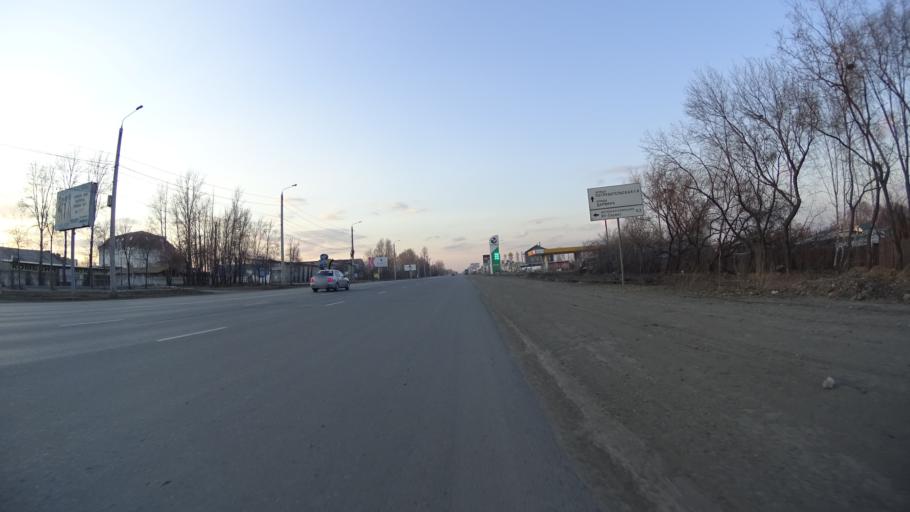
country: RU
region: Chelyabinsk
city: Novosineglazovskiy
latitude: 55.0871
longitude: 61.3885
